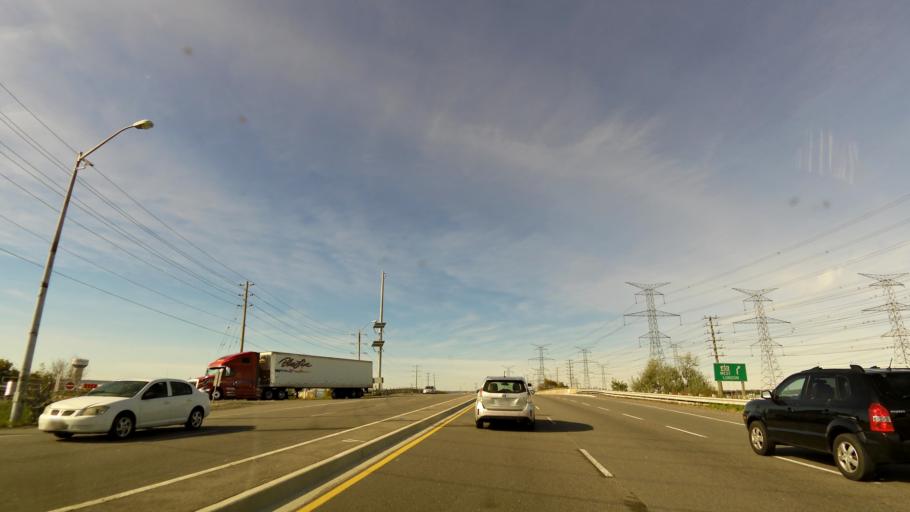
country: CA
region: Ontario
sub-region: Halton
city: Milton
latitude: 43.5412
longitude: -79.8614
